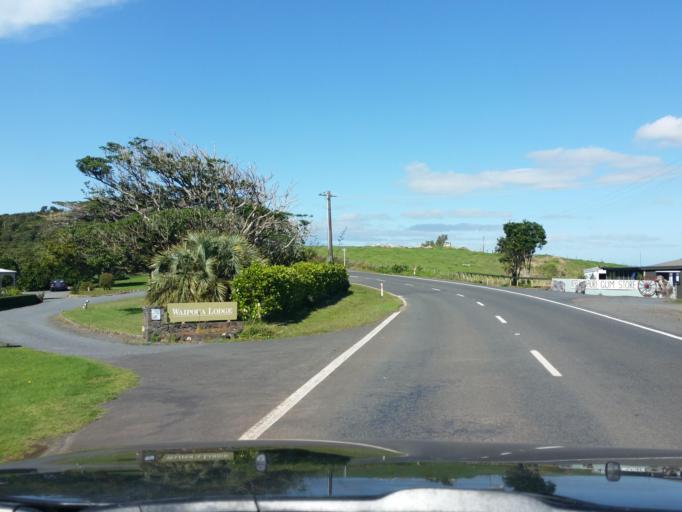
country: NZ
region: Northland
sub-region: Kaipara District
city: Dargaville
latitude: -35.6951
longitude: 173.5725
